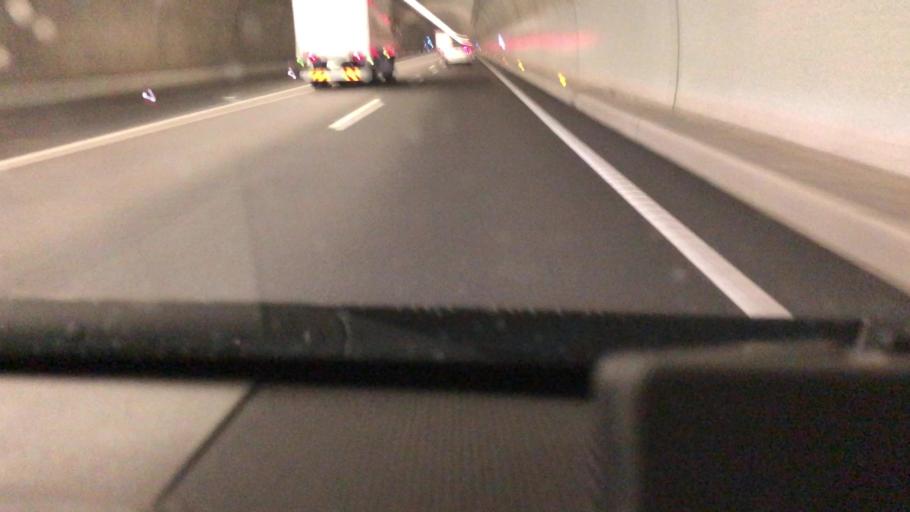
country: JP
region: Shizuoka
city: Kanaya
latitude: 34.8629
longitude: 138.1518
